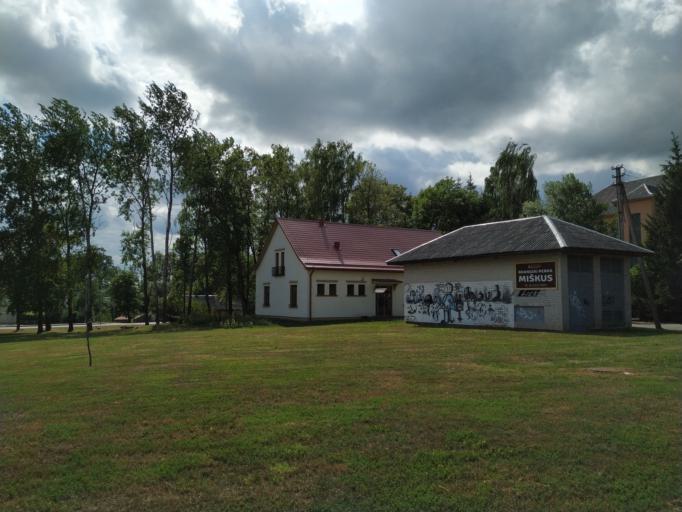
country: LT
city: Kupiskis
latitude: 55.8336
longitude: 24.9839
